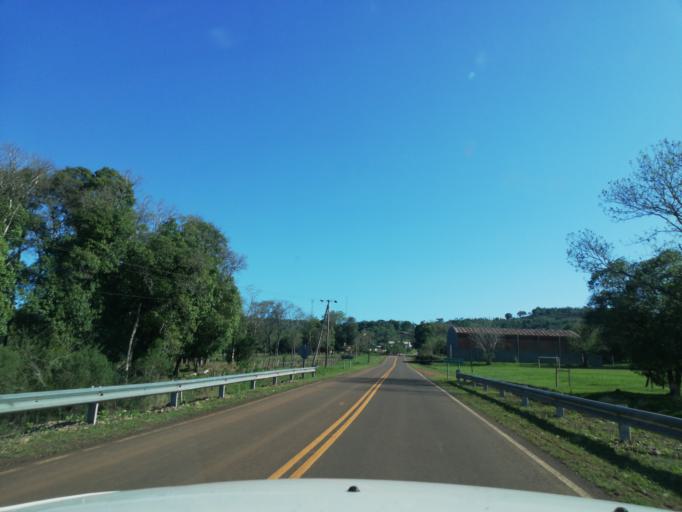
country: AR
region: Misiones
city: Arroyo del Medio
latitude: -27.6926
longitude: -55.4013
